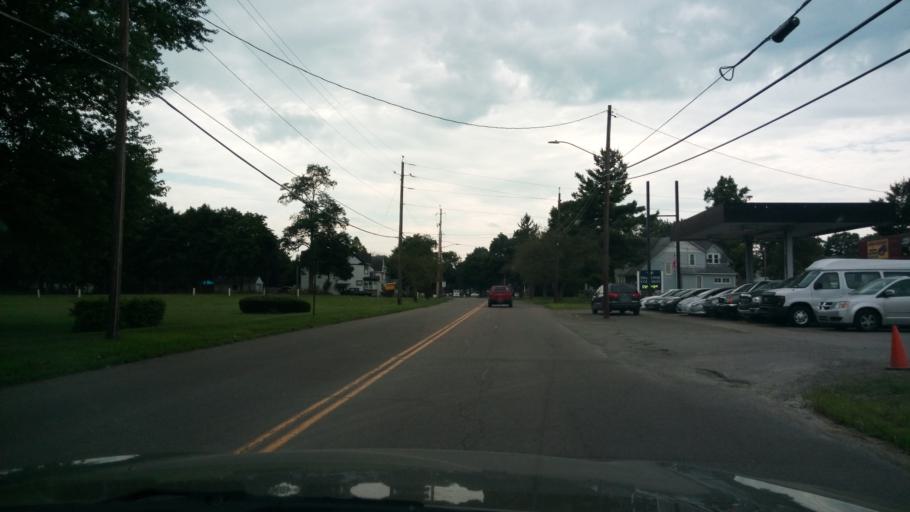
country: US
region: New York
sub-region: Chemung County
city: Elmira Heights
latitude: 42.1156
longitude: -76.8083
